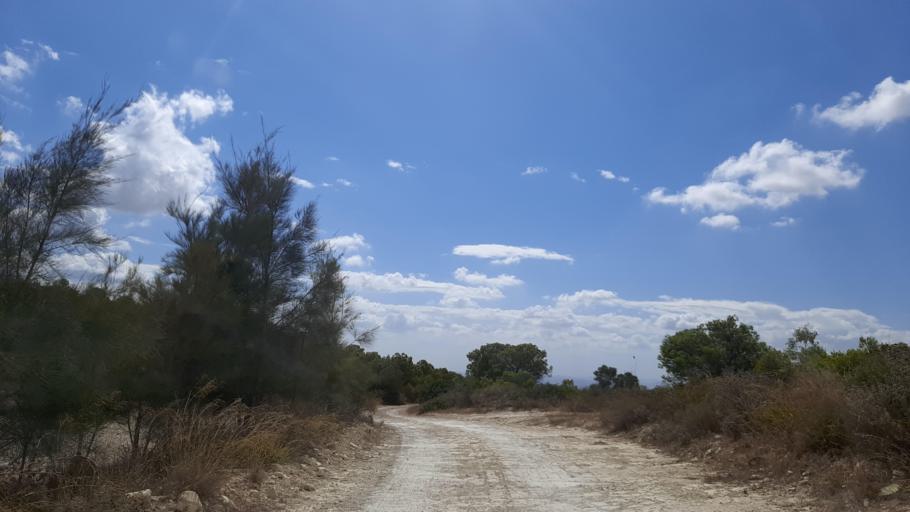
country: TN
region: Zaghwan
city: Zaghouan
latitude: 36.4967
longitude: 10.1728
